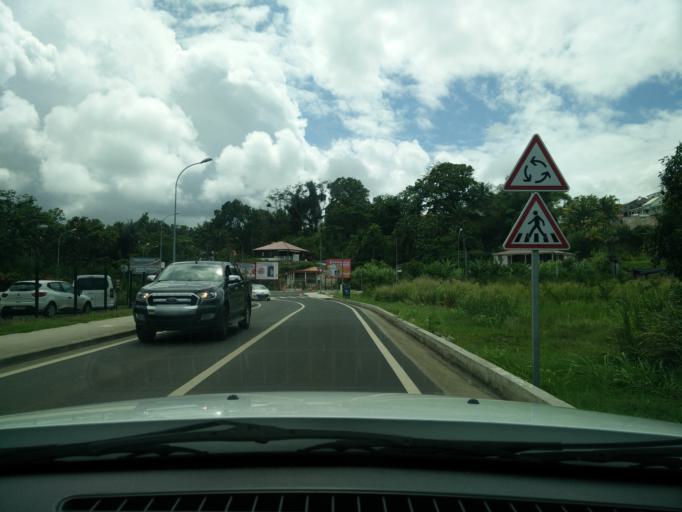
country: GP
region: Guadeloupe
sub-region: Guadeloupe
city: Petit-Bourg
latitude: 16.2031
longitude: -61.6084
